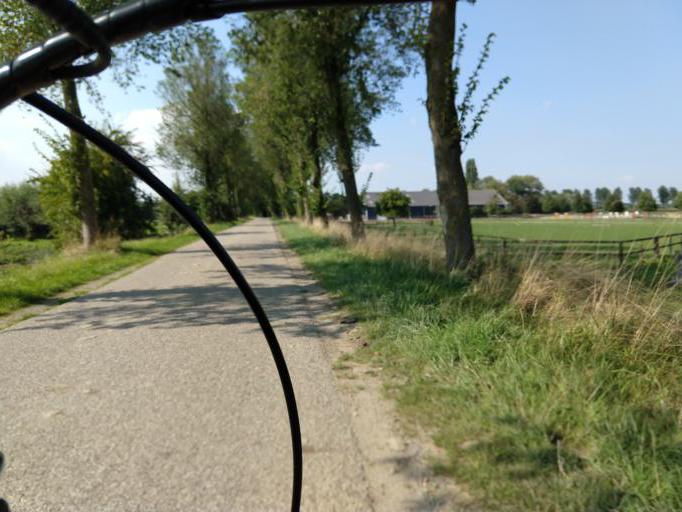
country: NL
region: Zeeland
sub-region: Gemeente Goes
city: Goes
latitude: 51.4358
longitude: 3.8365
